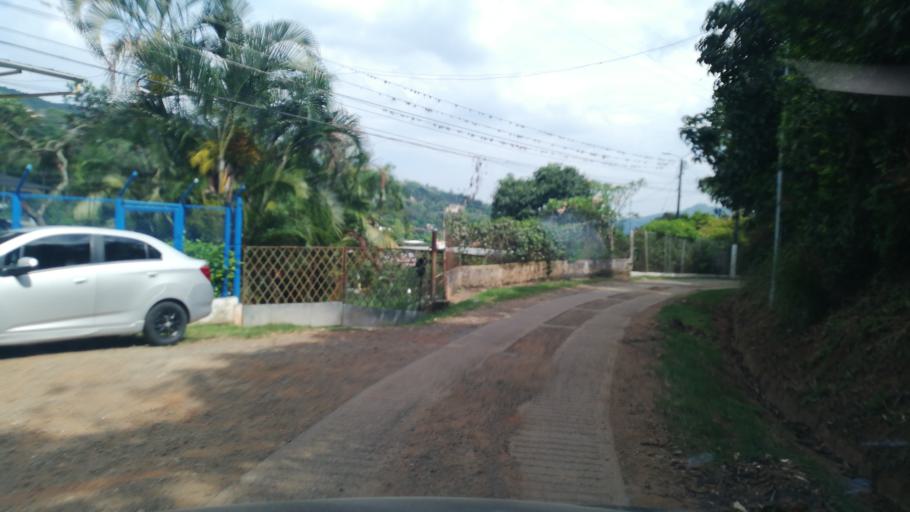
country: CO
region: Valle del Cauca
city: Cali
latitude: 3.4818
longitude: -76.5542
